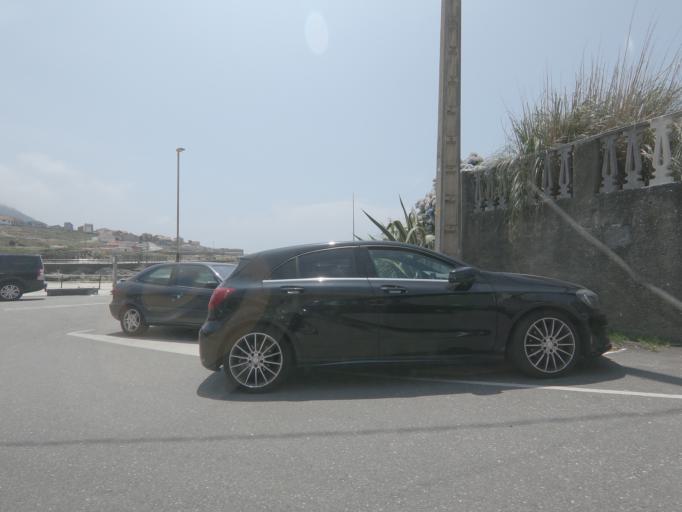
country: ES
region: Galicia
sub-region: Provincia de Pontevedra
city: A Guarda
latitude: 41.9106
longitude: -8.8766
